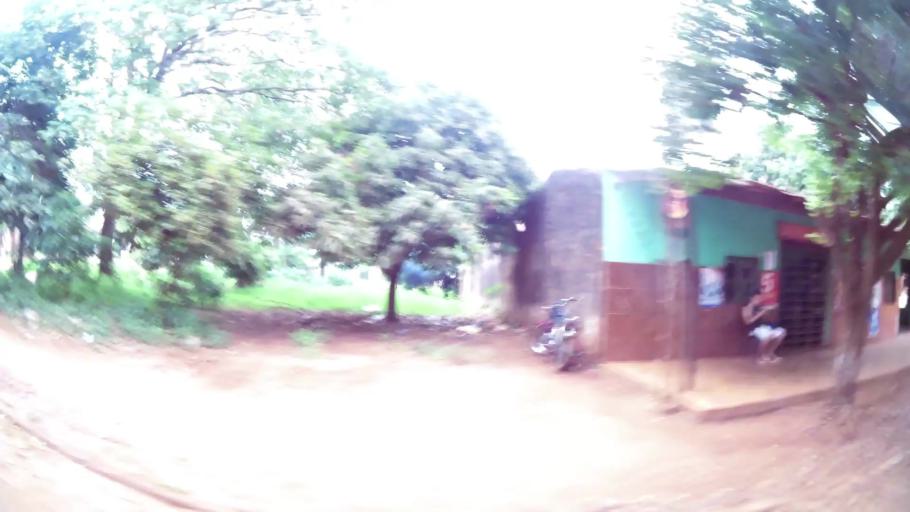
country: PY
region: Alto Parana
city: Presidente Franco
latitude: -25.5484
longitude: -54.6543
